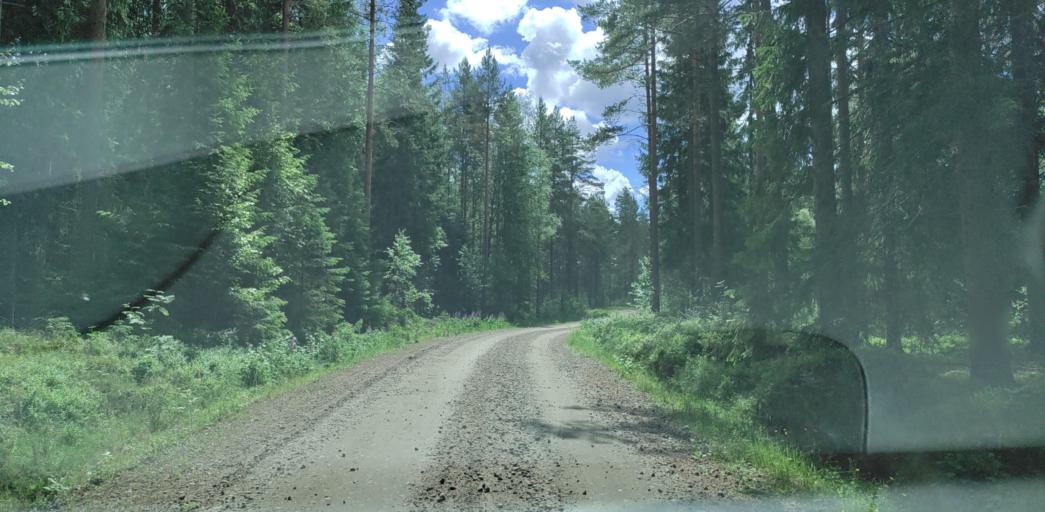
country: SE
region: Vaermland
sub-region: Hagfors Kommun
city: Ekshaerad
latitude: 60.0725
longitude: 13.3121
